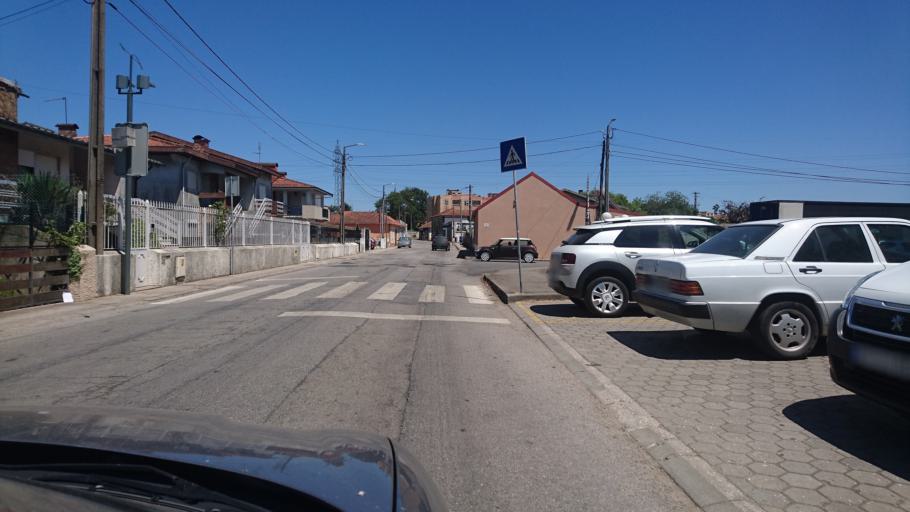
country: PT
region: Aveiro
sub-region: Santa Maria da Feira
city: Pacos de Brandao
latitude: 40.9842
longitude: -8.6011
